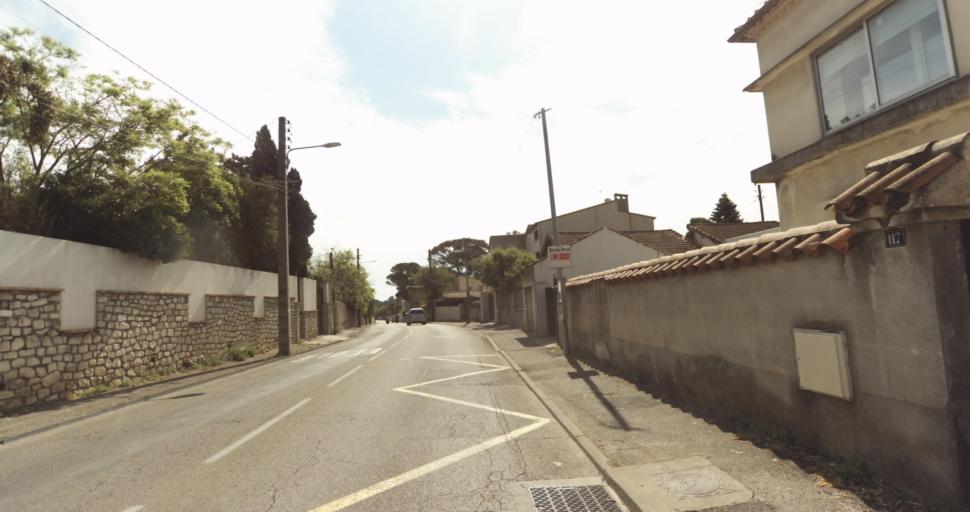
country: FR
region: Languedoc-Roussillon
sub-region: Departement du Gard
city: Nimes
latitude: 43.8371
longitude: 4.3304
